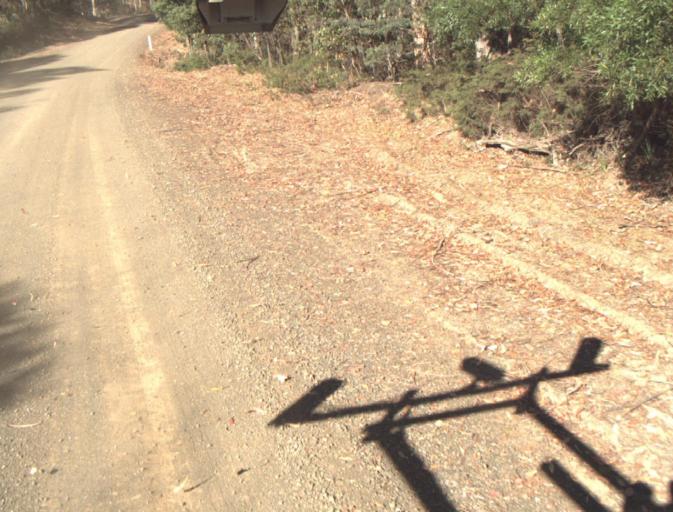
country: AU
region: Tasmania
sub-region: Launceston
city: Newstead
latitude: -41.3013
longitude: 147.3338
